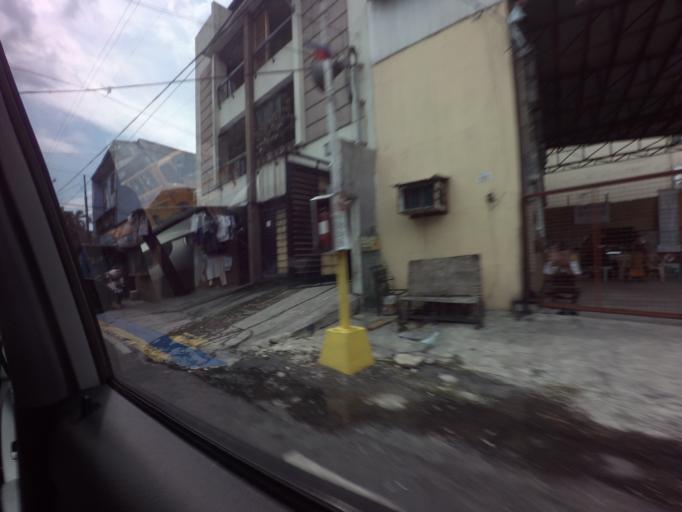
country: PH
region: Metro Manila
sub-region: City of Manila
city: Quiapo
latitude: 14.6036
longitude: 121.0080
